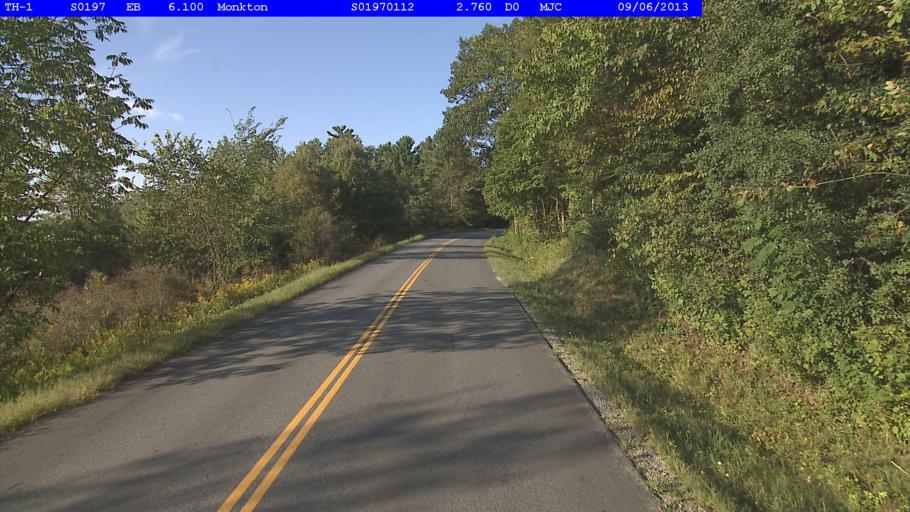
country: US
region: Vermont
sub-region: Addison County
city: Vergennes
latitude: 44.2178
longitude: -73.1550
